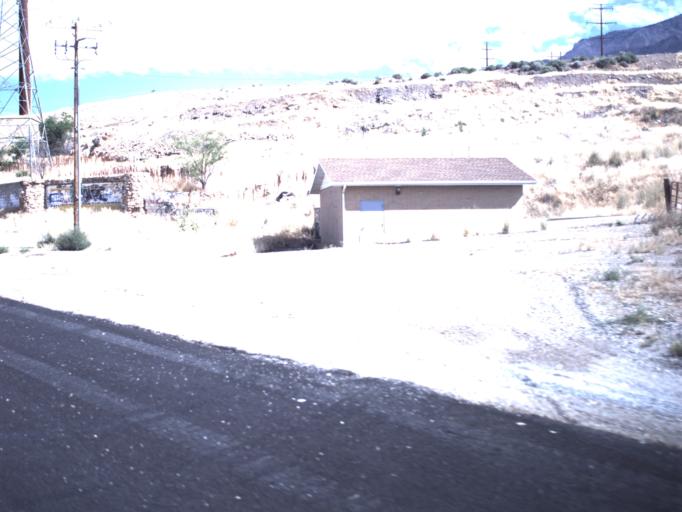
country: US
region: Utah
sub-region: Box Elder County
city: South Willard
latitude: 41.3359
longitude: -112.0276
